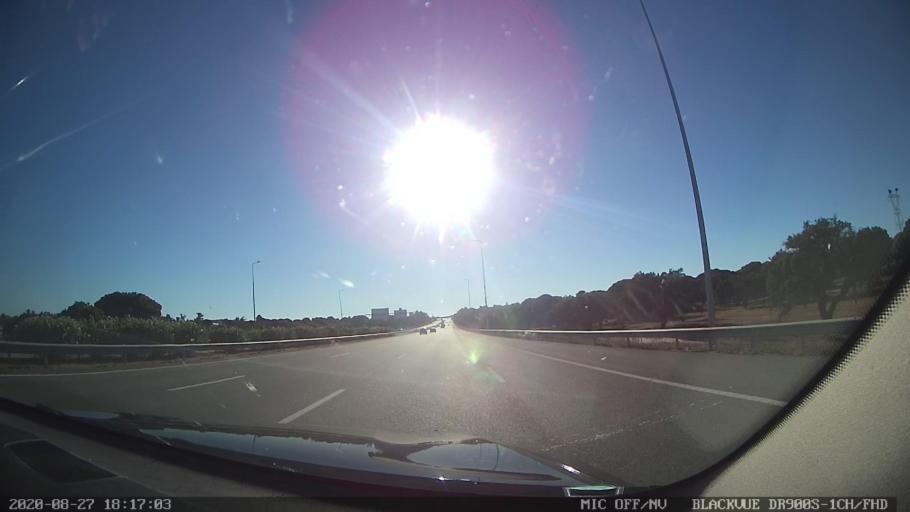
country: PT
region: Evora
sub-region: Vendas Novas
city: Vendas Novas
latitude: 38.6032
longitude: -8.6551
